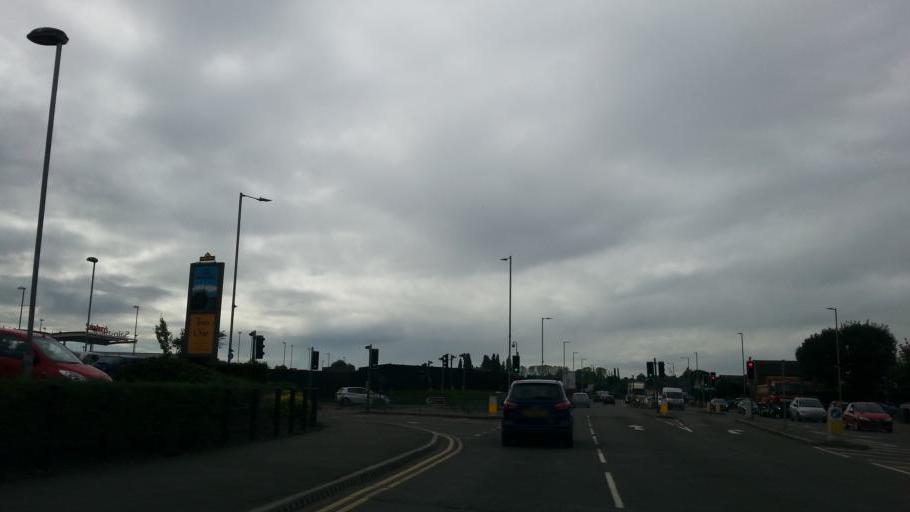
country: GB
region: England
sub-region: Gloucestershire
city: Gloucester
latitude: 51.8599
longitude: -2.2590
